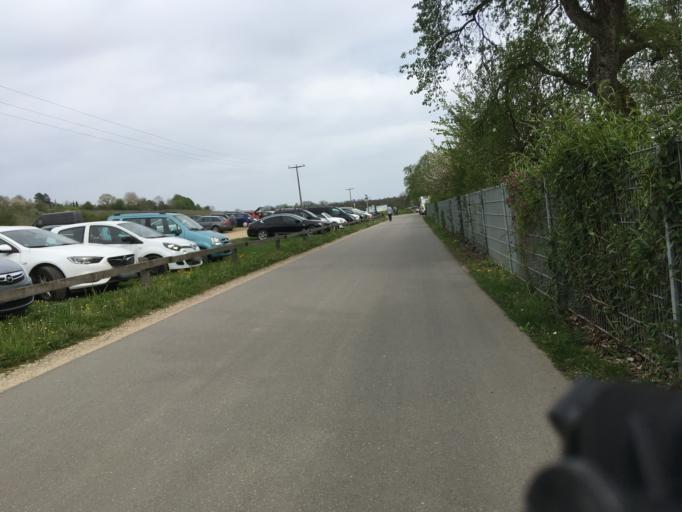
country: DE
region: Baden-Wuerttemberg
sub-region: Freiburg Region
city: Gailingen
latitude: 47.6900
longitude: 8.7595
